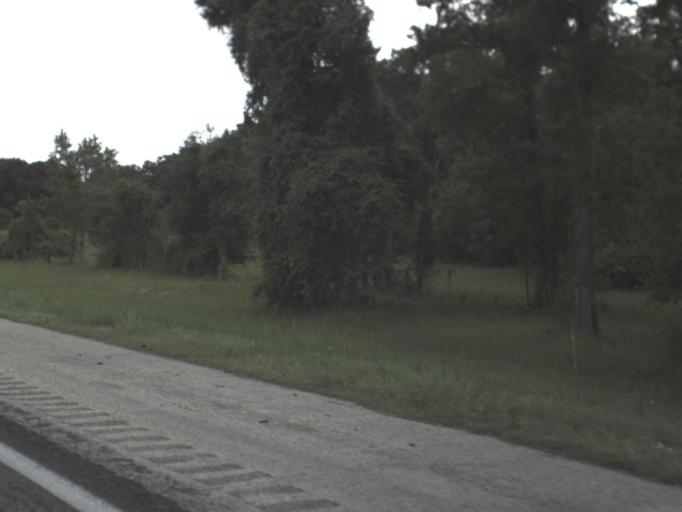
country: US
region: Florida
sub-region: Alachua County
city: High Springs
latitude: 29.9090
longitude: -82.5512
